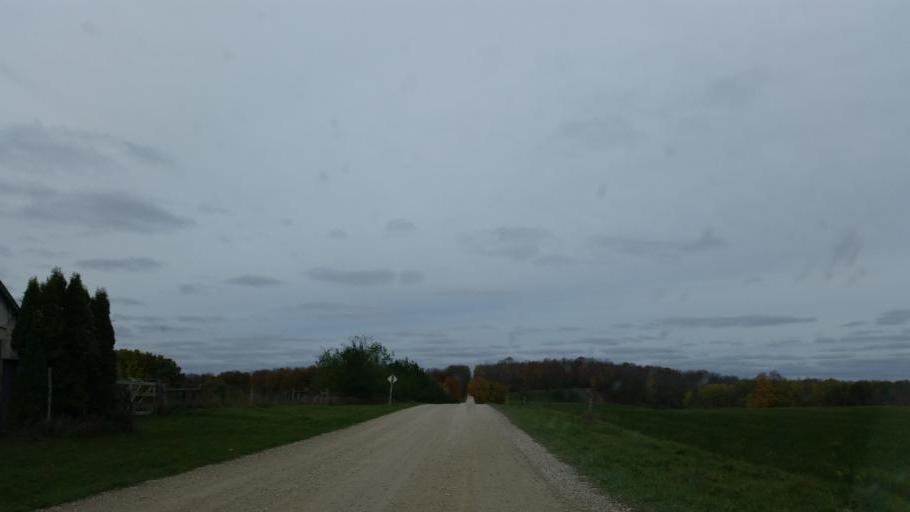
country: CA
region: Ontario
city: Wingham
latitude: 43.9789
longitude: -81.3331
